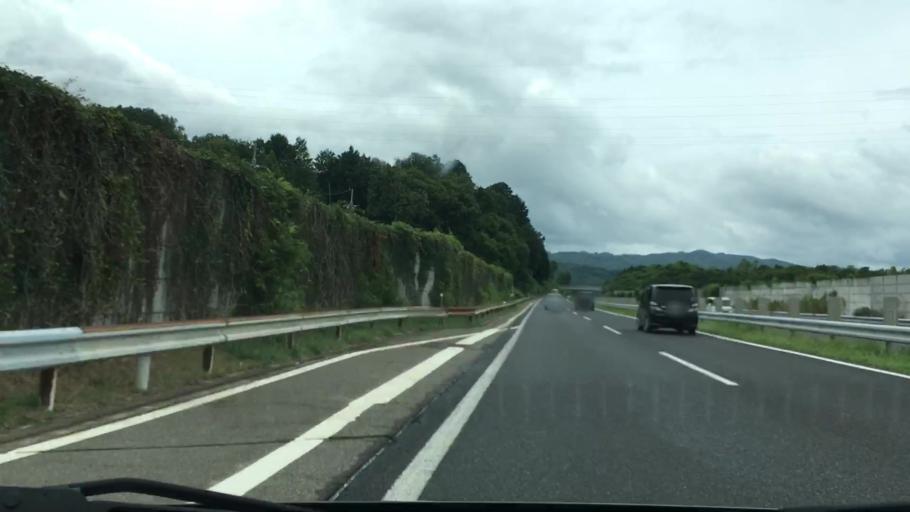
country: JP
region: Okayama
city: Tsuyama
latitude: 35.0604
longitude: 133.9322
